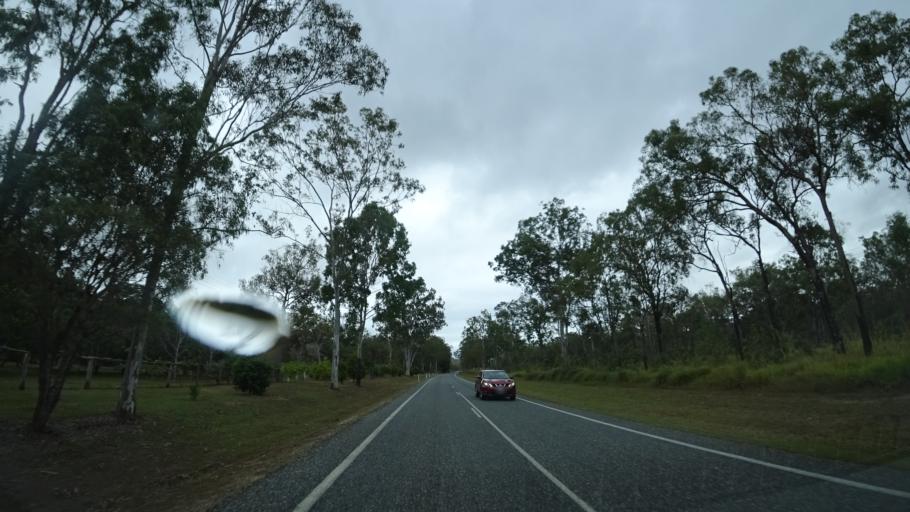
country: AU
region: Queensland
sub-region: Cairns
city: Port Douglas
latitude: -16.7306
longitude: 145.3522
